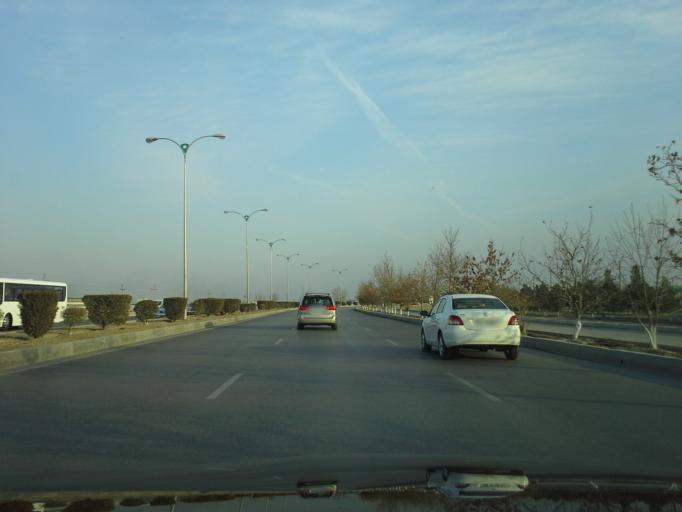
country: TM
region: Ahal
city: Abadan
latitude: 38.0566
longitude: 58.1798
